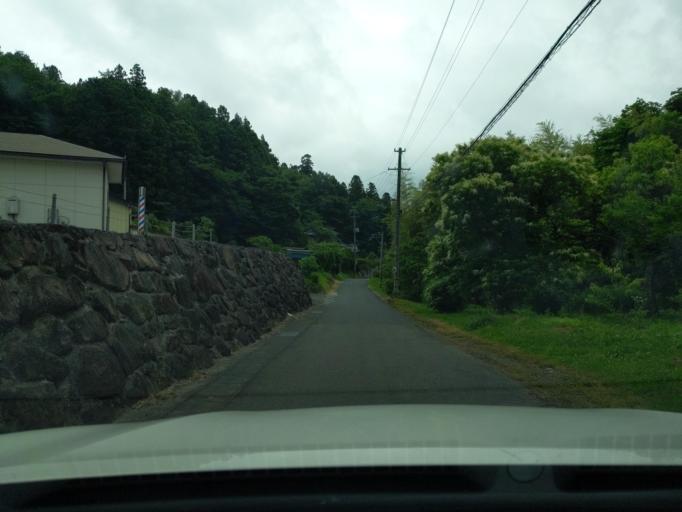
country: JP
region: Fukushima
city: Miharu
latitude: 37.4054
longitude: 140.4439
